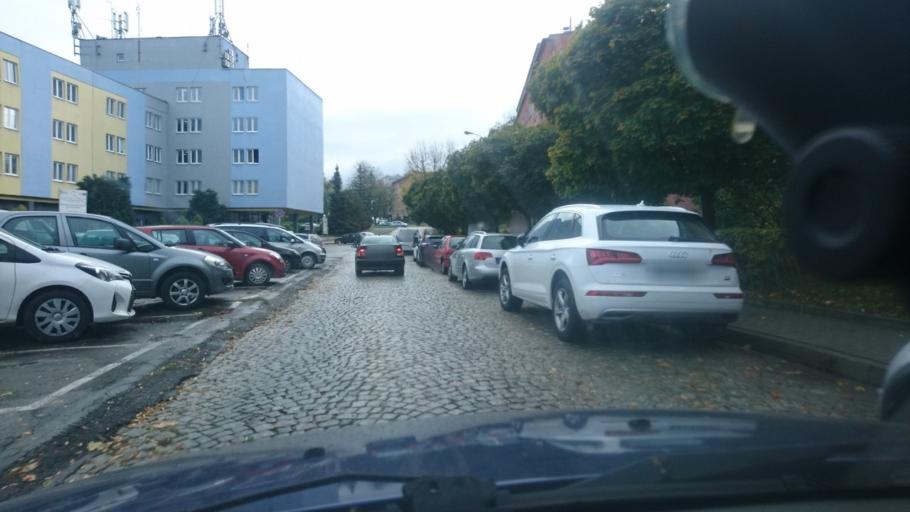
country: PL
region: Silesian Voivodeship
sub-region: Bielsko-Biala
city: Bielsko-Biala
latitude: 49.8265
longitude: 19.0304
